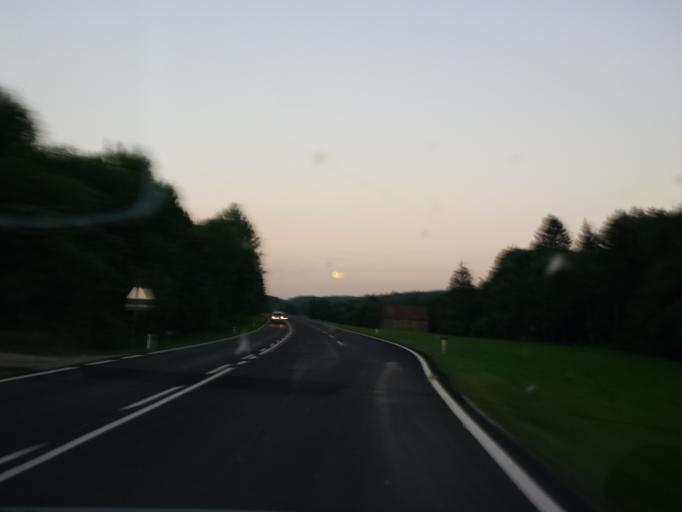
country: AT
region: Lower Austria
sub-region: Politischer Bezirk Lilienfeld
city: Ramsau
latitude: 48.0337
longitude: 15.8333
